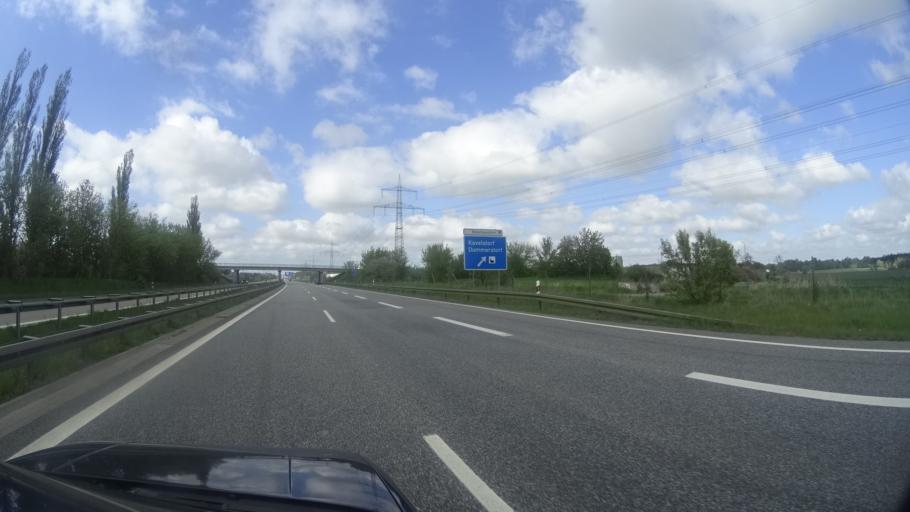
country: DE
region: Mecklenburg-Vorpommern
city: Kavelstorf
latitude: 54.0092
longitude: 12.2032
